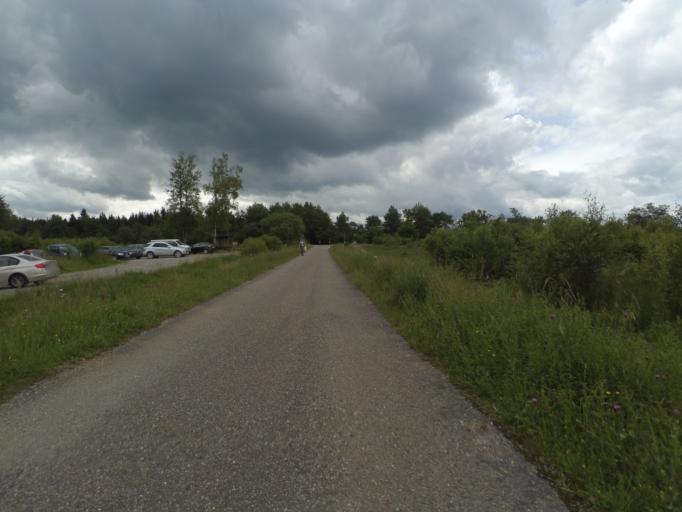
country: DE
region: North Rhine-Westphalia
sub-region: Regierungsbezirk Koln
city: Monschau
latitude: 50.5686
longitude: 6.1804
